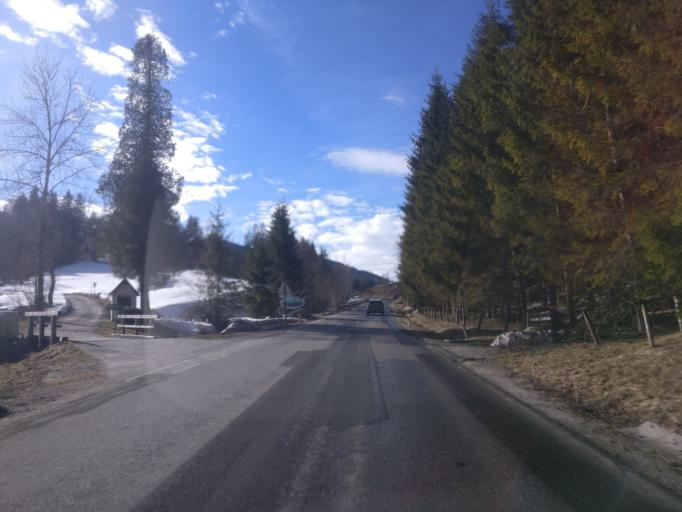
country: AT
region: Styria
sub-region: Politischer Bezirk Liezen
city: Landl
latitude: 47.6544
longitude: 14.6685
